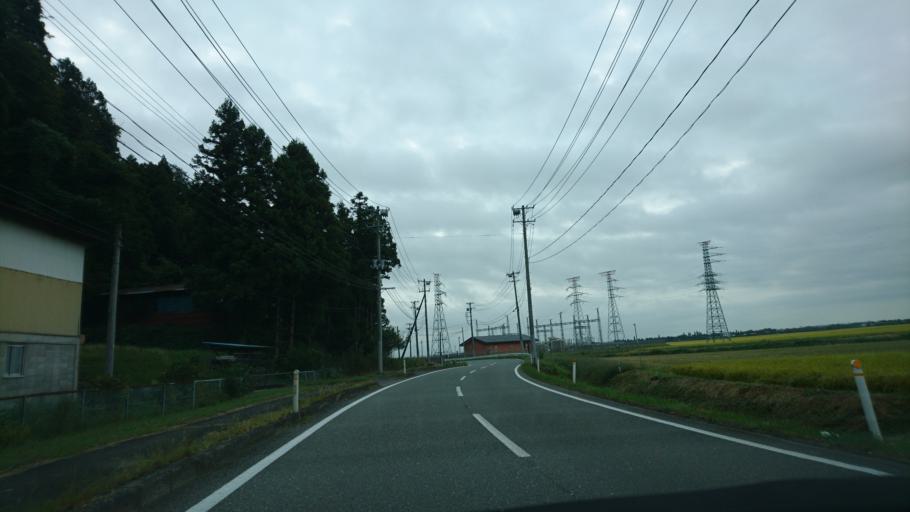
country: JP
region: Iwate
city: Ichinoseki
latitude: 38.8090
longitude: 141.0841
